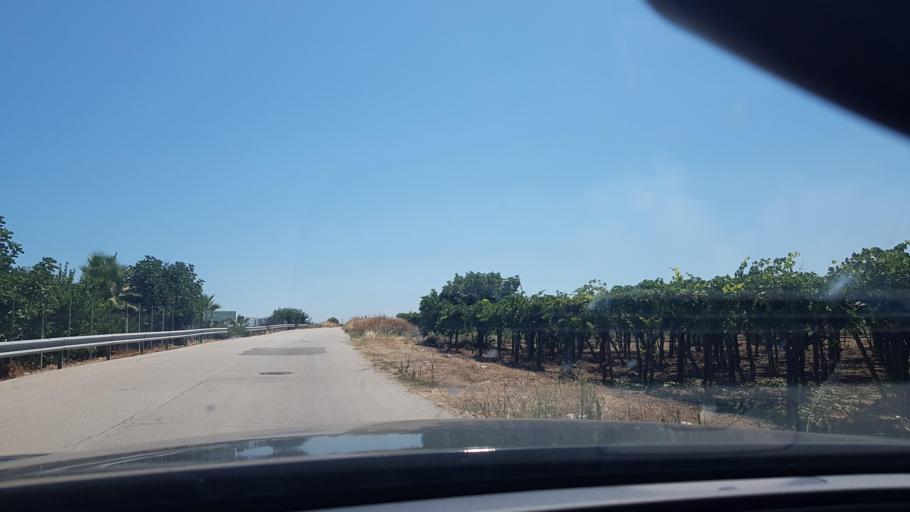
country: IT
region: Apulia
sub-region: Provincia di Barletta - Andria - Trani
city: Barletta
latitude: 41.3088
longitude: 16.3255
